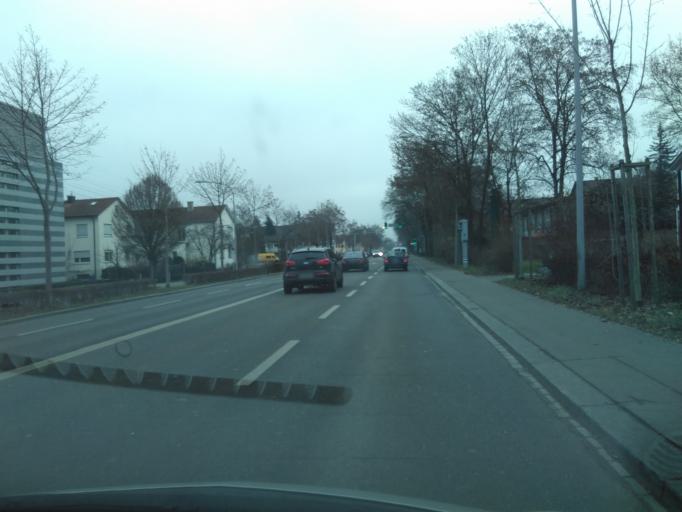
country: CH
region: Zurich
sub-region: Bezirk Zuerich
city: Zuerich (Kreis 12) / Schwamendingen-Mitte
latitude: 47.4101
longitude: 8.5742
